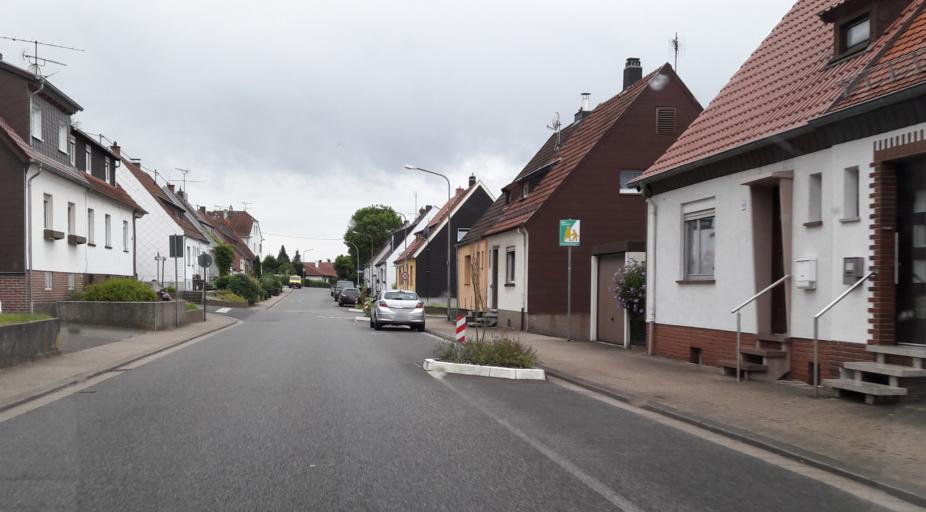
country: DE
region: Saarland
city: Spiesen-Elversberg
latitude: 49.3119
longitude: 7.1444
